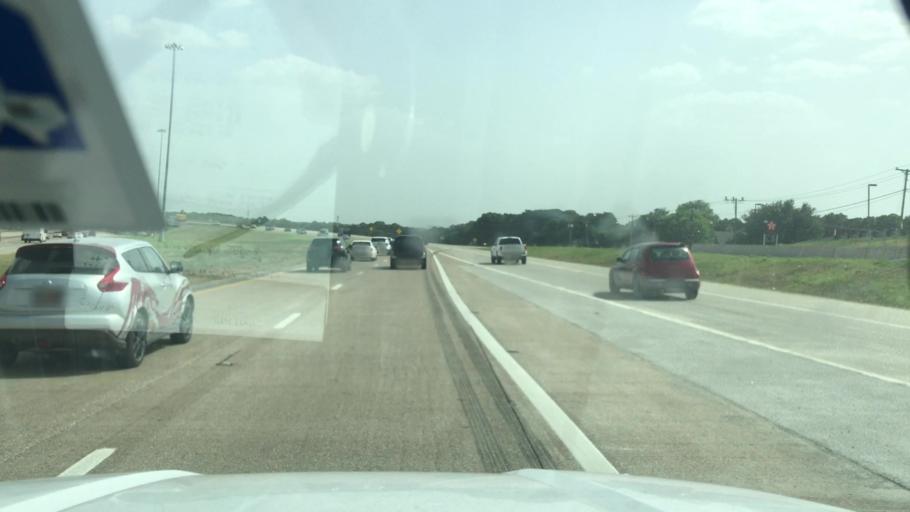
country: US
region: Texas
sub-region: Tarrant County
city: Grapevine
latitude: 32.9104
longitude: -97.0993
